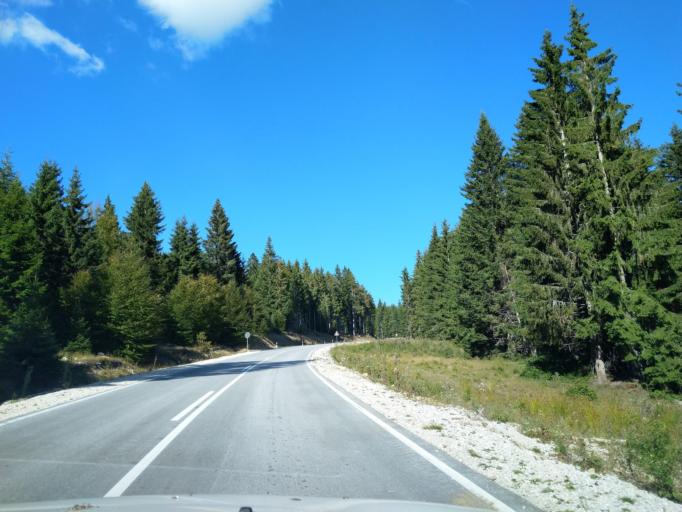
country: RS
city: Sokolovica
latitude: 43.3002
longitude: 20.3072
